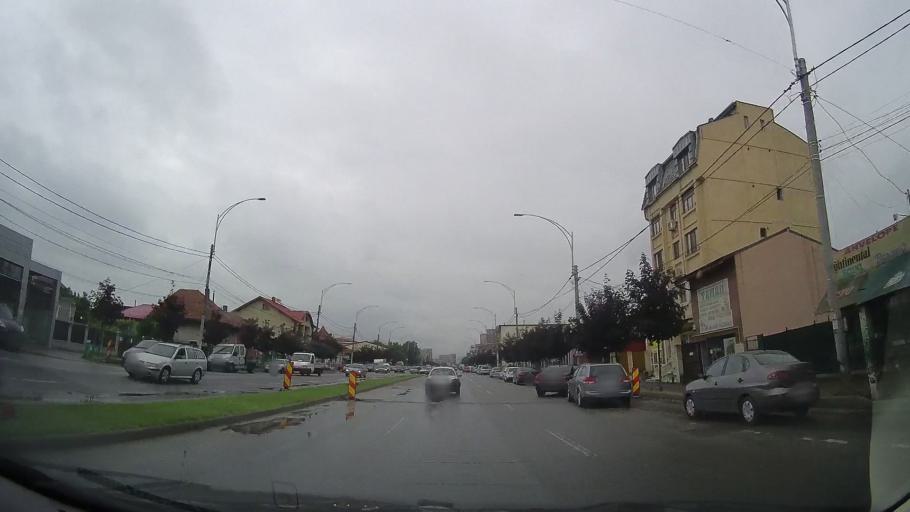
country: RO
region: Mehedinti
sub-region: Municipiul Drobeta-Turnu Severin
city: Drobeta-Turnu Severin
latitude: 44.6314
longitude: 22.6482
